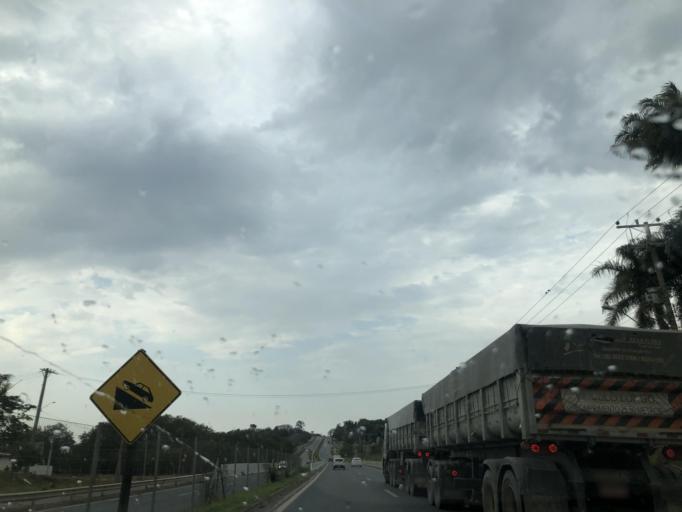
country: BR
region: Sao Paulo
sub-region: Salto De Pirapora
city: Salto de Pirapora
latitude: -23.6377
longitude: -47.5729
